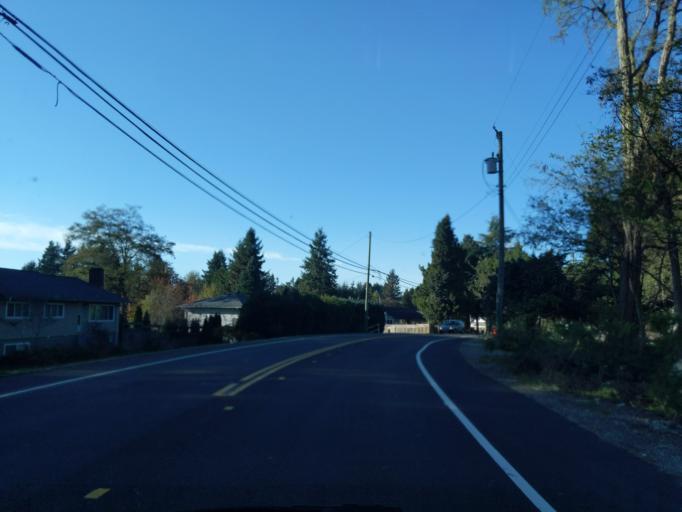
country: CA
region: British Columbia
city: New Westminster
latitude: 49.1892
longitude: -122.8611
